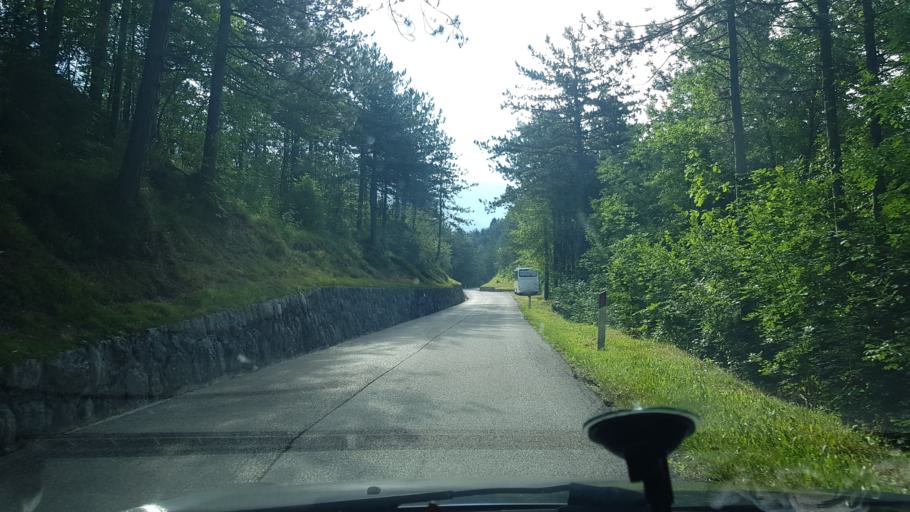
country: IT
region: Friuli Venezia Giulia
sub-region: Provincia di Udine
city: Prato
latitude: 46.3646
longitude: 13.3323
